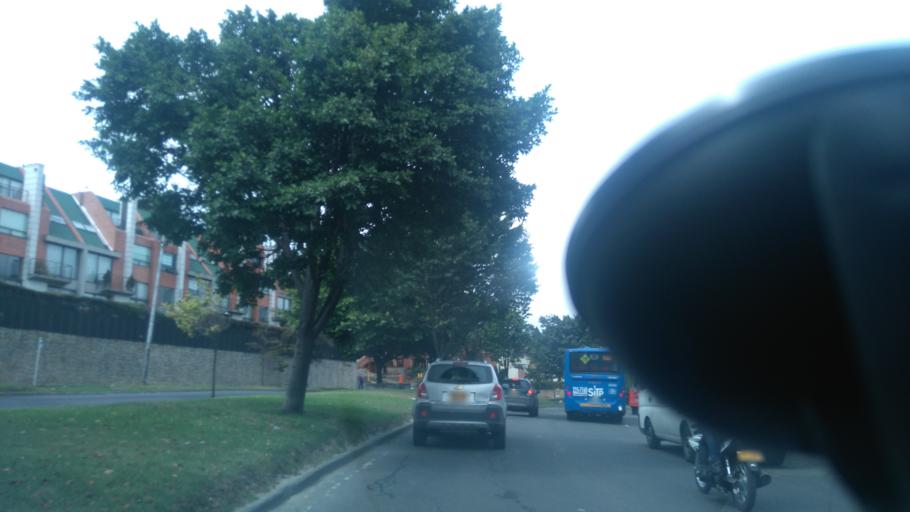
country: CO
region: Cundinamarca
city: La Calera
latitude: 4.7258
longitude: -74.0249
